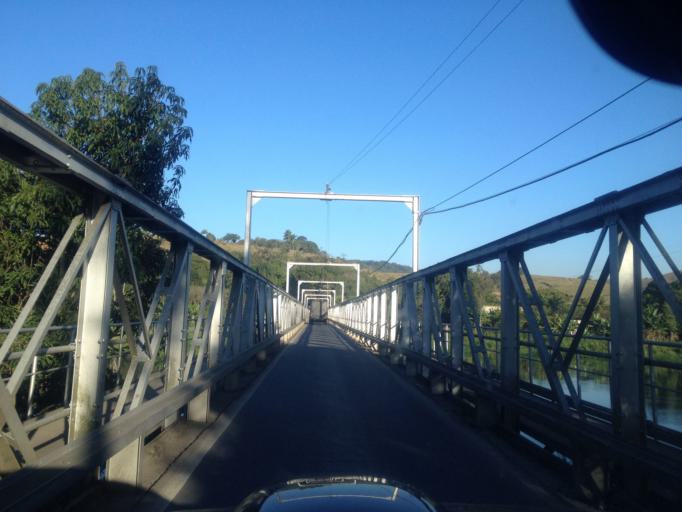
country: BR
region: Rio de Janeiro
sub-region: Porto Real
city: Porto Real
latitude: -22.4241
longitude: -44.2844
